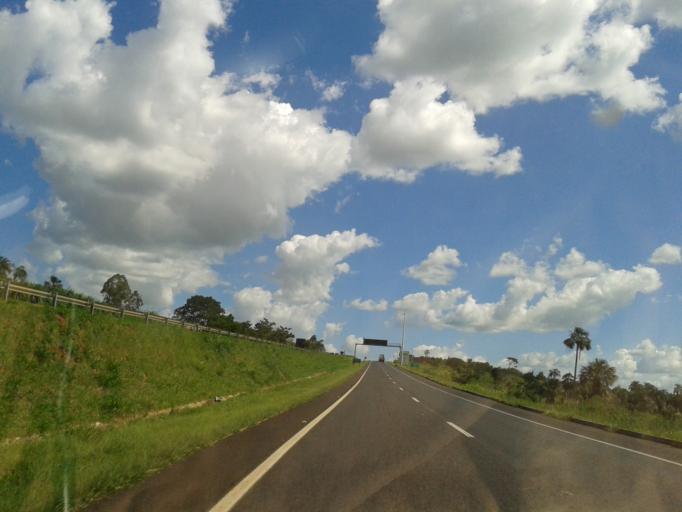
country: BR
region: Goias
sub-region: Morrinhos
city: Morrinhos
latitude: -17.6904
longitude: -49.1575
